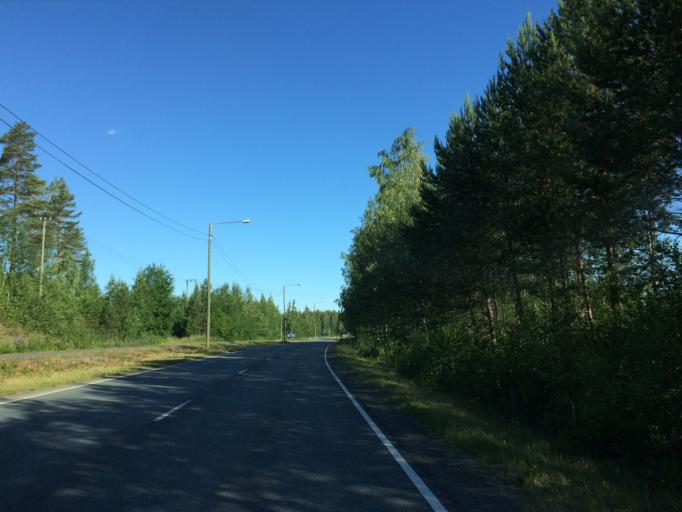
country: FI
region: Haeme
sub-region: Haemeenlinna
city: Haemeenlinna
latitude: 60.9620
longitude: 24.4527
